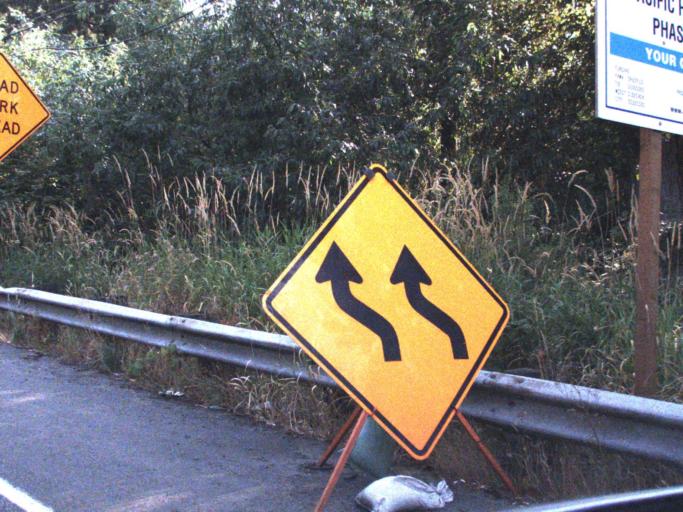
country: US
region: Washington
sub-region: Pierce County
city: Fife Heights
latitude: 47.2792
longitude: -122.3241
